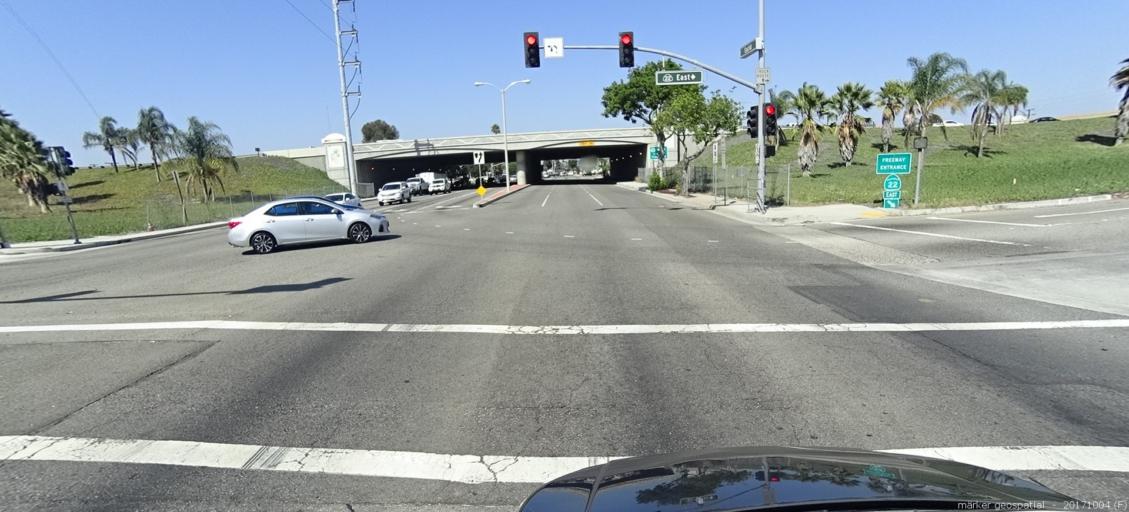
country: US
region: California
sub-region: Orange County
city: Garden Grove
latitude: 33.7651
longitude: -117.9377
